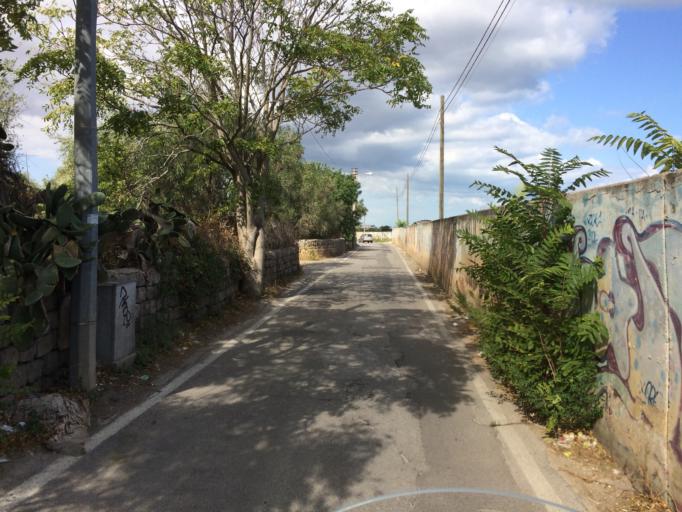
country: IT
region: Apulia
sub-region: Provincia di Bari
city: Bari
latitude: 41.1065
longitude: 16.8490
